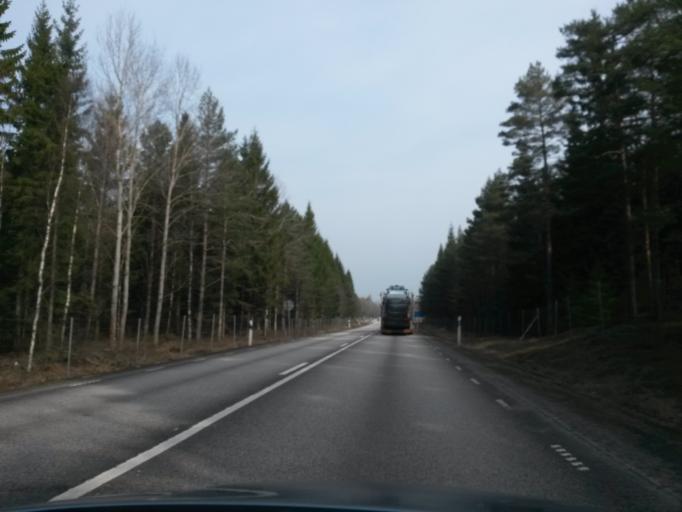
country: SE
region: Vaestra Goetaland
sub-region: Gullspangs Kommun
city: Hova
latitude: 58.8426
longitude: 14.1946
